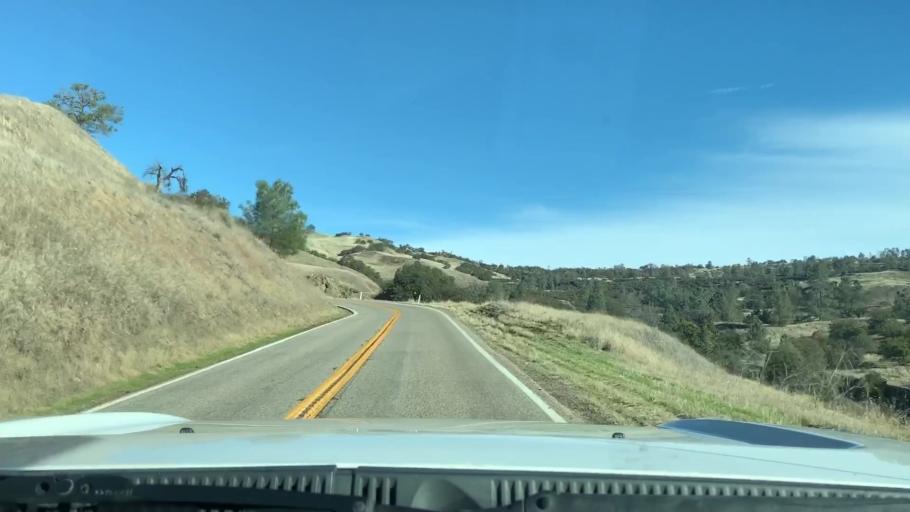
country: US
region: California
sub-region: Monterey County
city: King City
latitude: 36.1912
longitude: -120.7998
